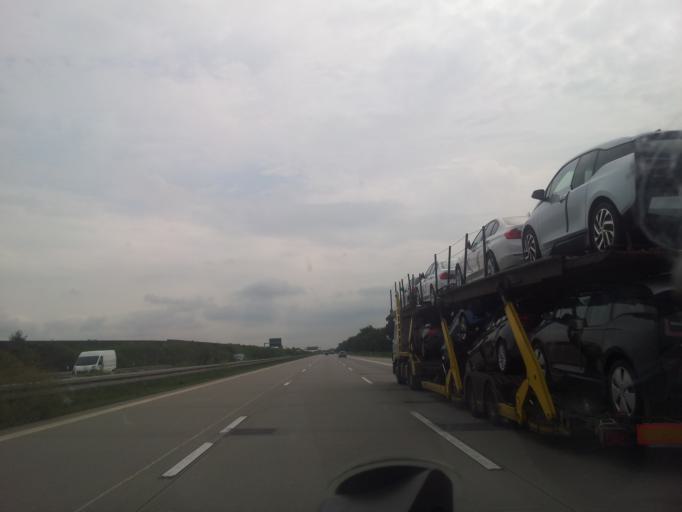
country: DE
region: Saxony
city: Schkeuditz
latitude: 51.4191
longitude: 12.2601
